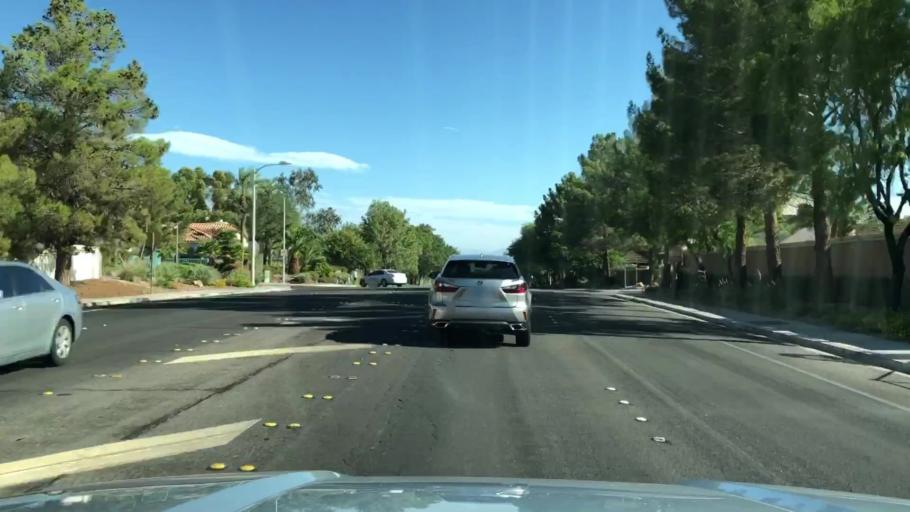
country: US
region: Nevada
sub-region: Clark County
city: Whitney
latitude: 36.0379
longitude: -115.0688
